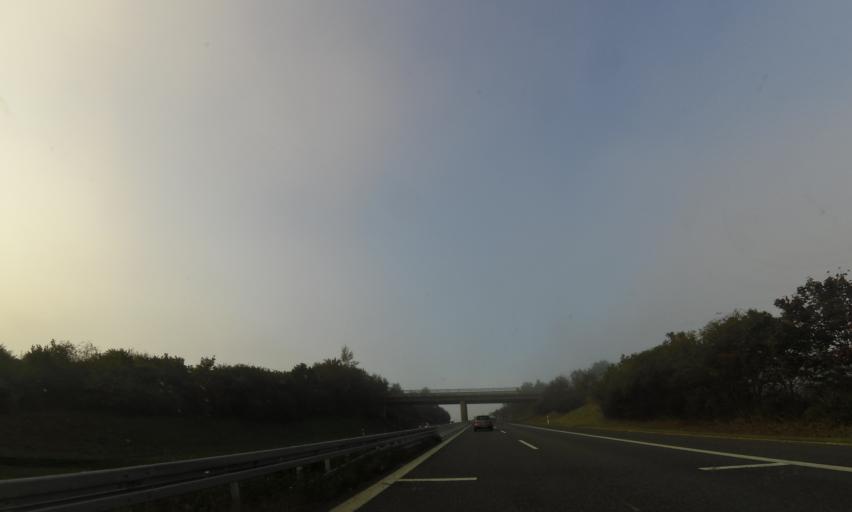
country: DE
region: Saxony
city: Neuensalz
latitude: 50.4936
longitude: 12.1927
